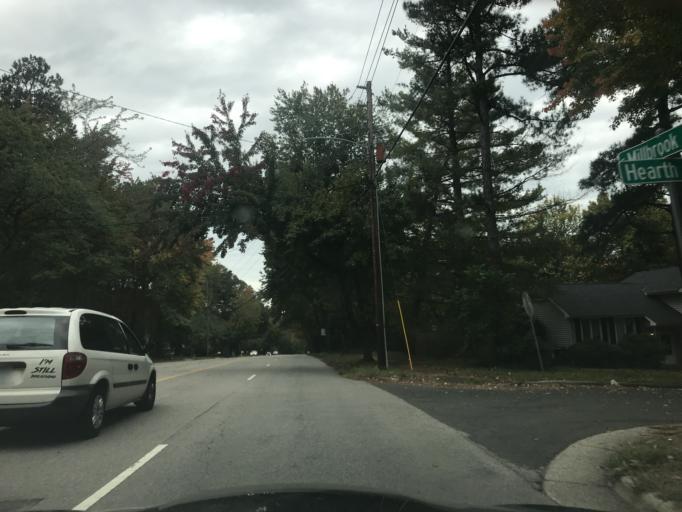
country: US
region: North Carolina
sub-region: Wake County
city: West Raleigh
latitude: 35.8507
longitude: -78.6166
